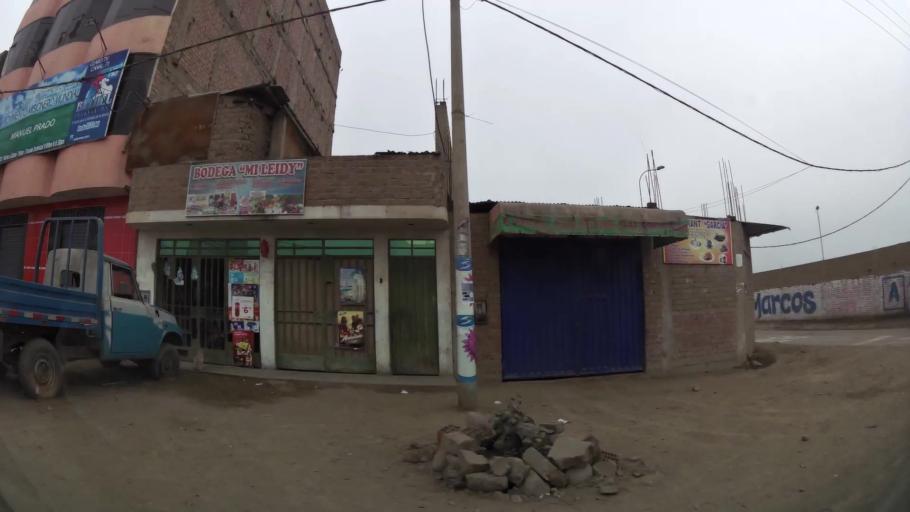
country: PE
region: Lima
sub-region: Lima
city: Urb. Santo Domingo
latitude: -11.8640
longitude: -77.0222
